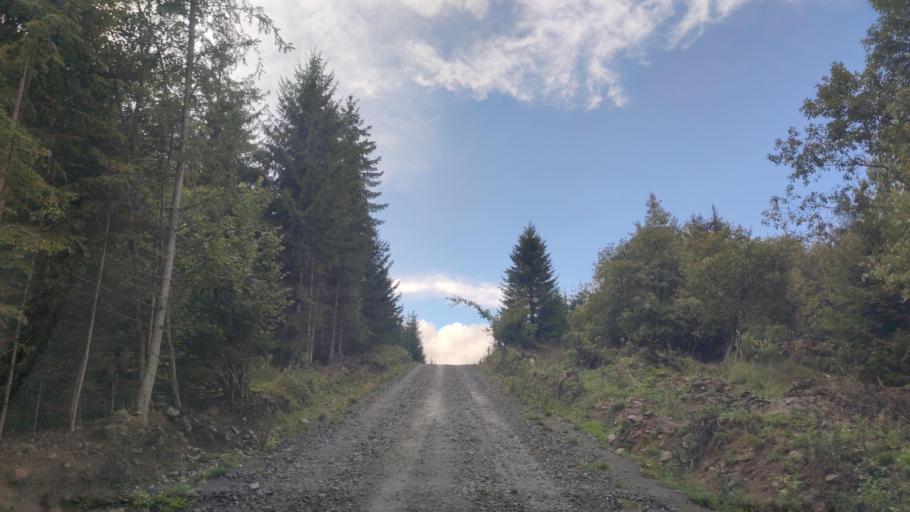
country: RO
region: Harghita
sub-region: Comuna Remetea
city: Remetea
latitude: 46.8162
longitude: 25.3555
